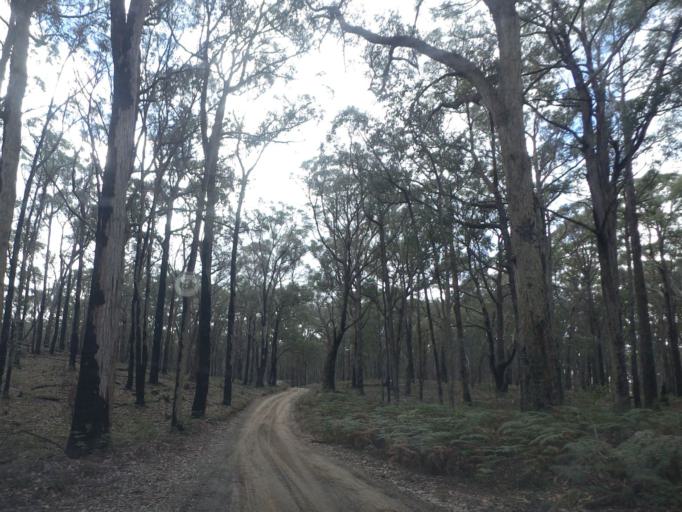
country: AU
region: Victoria
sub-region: Moorabool
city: Bacchus Marsh
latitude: -37.4582
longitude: 144.3207
